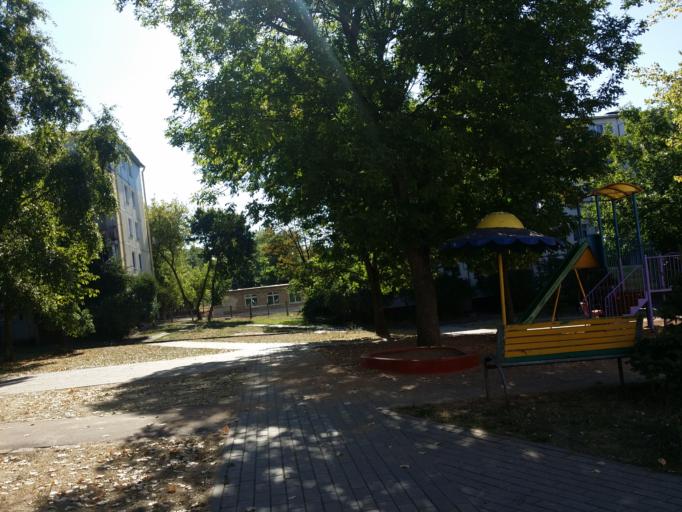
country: BY
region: Minsk
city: Minsk
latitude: 53.8747
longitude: 27.6224
